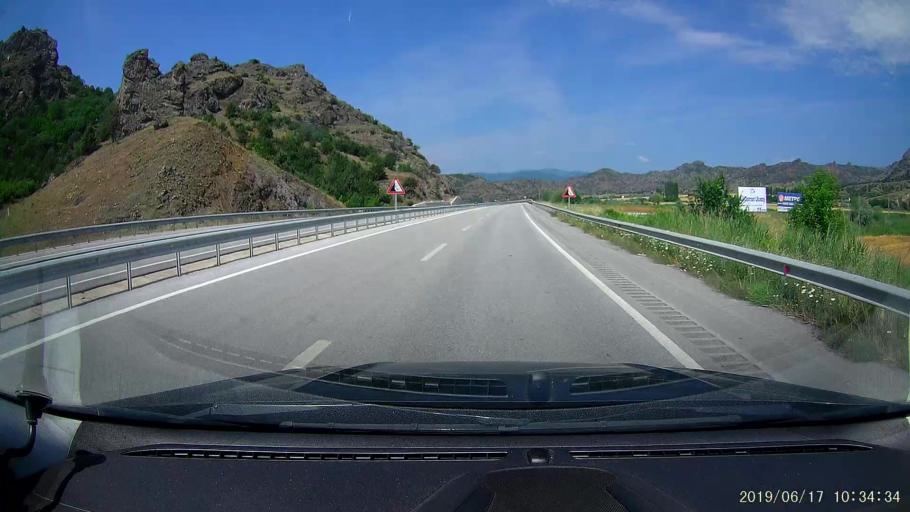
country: TR
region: Corum
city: Osmancik
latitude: 40.9814
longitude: 34.7220
